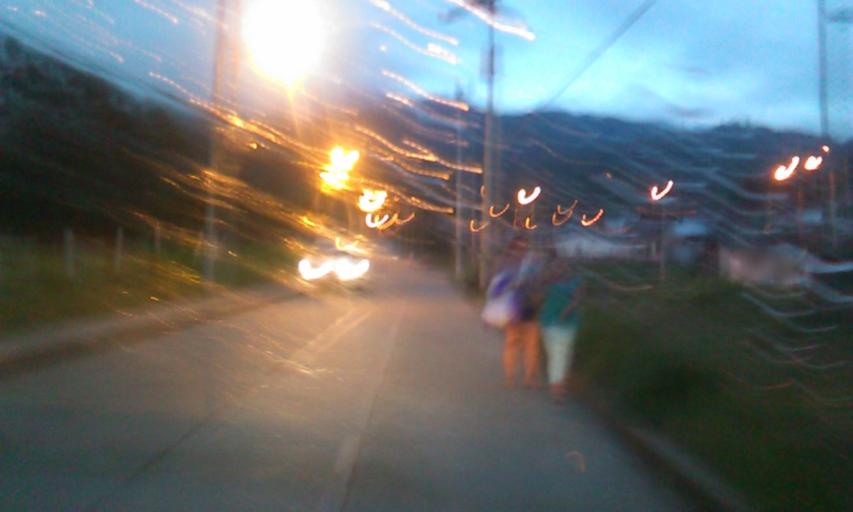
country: CO
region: Quindio
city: Cordoba
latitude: 4.3933
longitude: -75.6893
